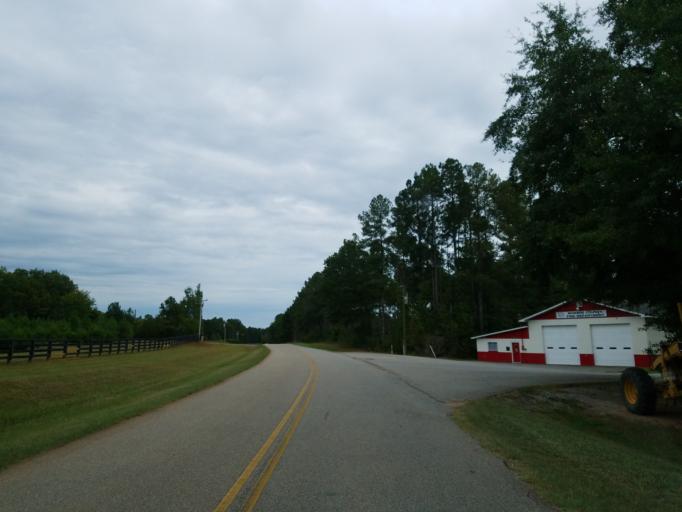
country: US
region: Georgia
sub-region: Monroe County
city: Forsyth
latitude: 32.9789
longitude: -84.0057
